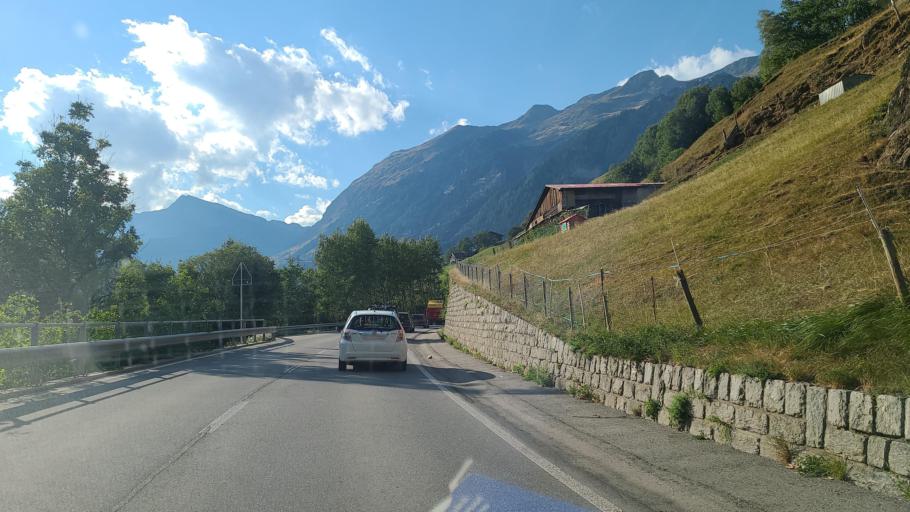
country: CH
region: Ticino
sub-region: Leventina District
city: Airolo
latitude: 46.5221
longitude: 8.6361
